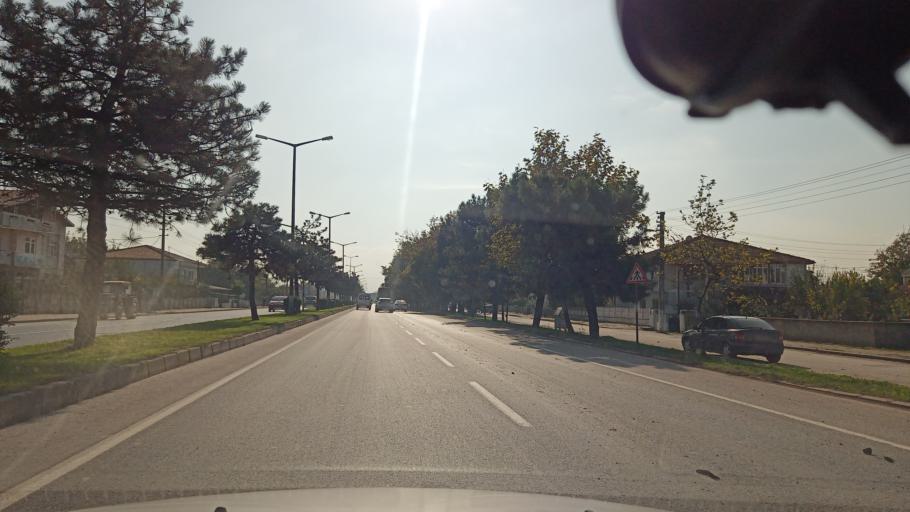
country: TR
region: Sakarya
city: Adapazari
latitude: 40.8088
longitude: 30.4054
